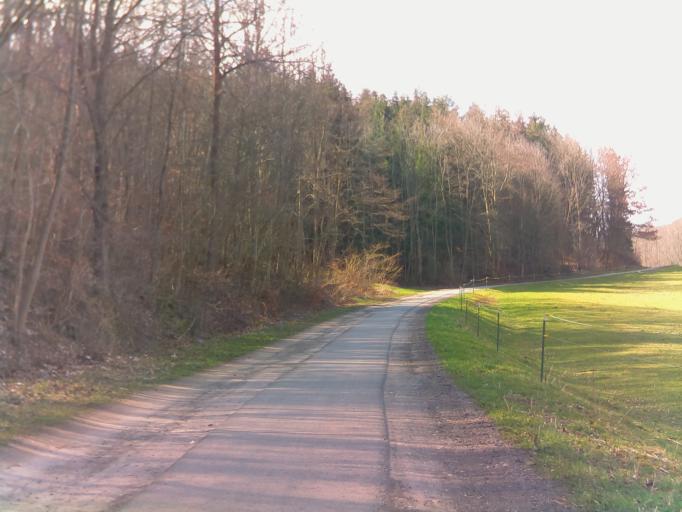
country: DE
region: Thuringia
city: Altenberga
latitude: 50.8296
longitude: 11.5159
